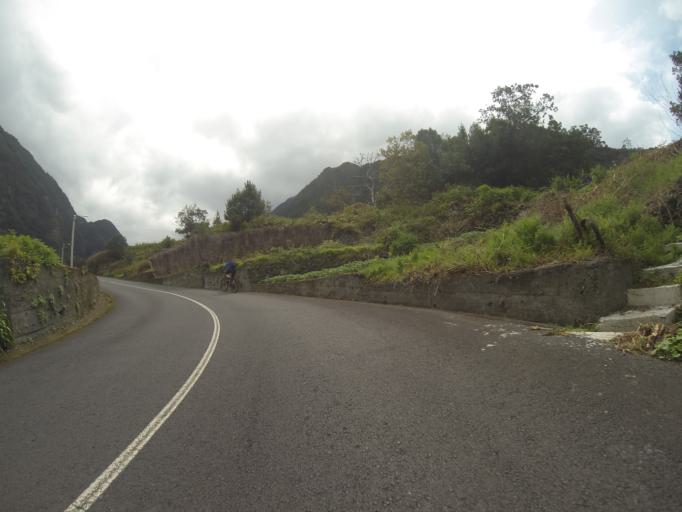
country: PT
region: Madeira
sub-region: Porto Moniz
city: Porto Moniz
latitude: 32.8196
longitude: -17.1095
